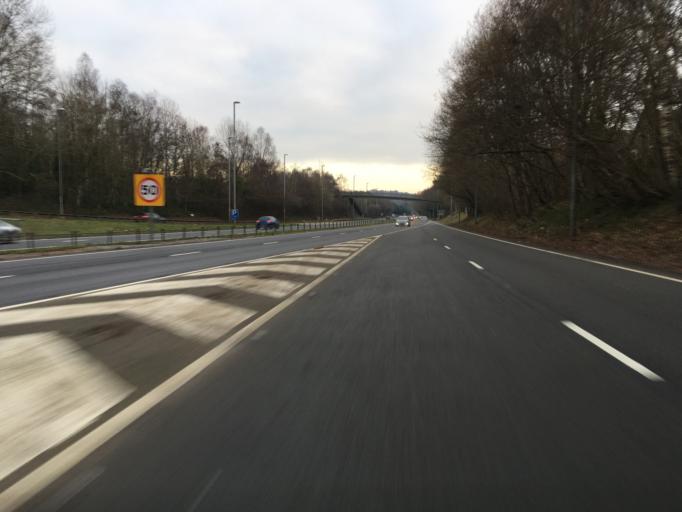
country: GB
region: Wales
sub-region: Newport
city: Newport
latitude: 51.5843
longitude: -3.0511
